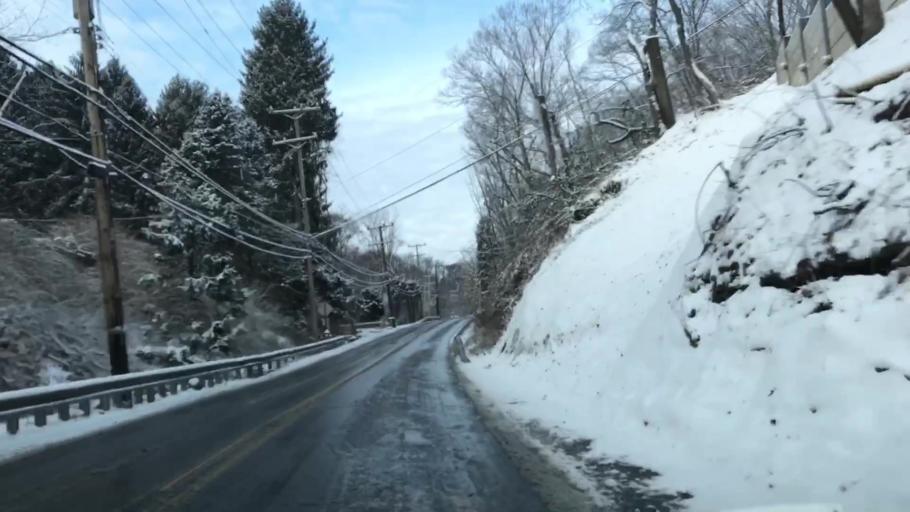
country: US
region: Pennsylvania
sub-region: Allegheny County
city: West View
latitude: 40.5387
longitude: -80.0526
